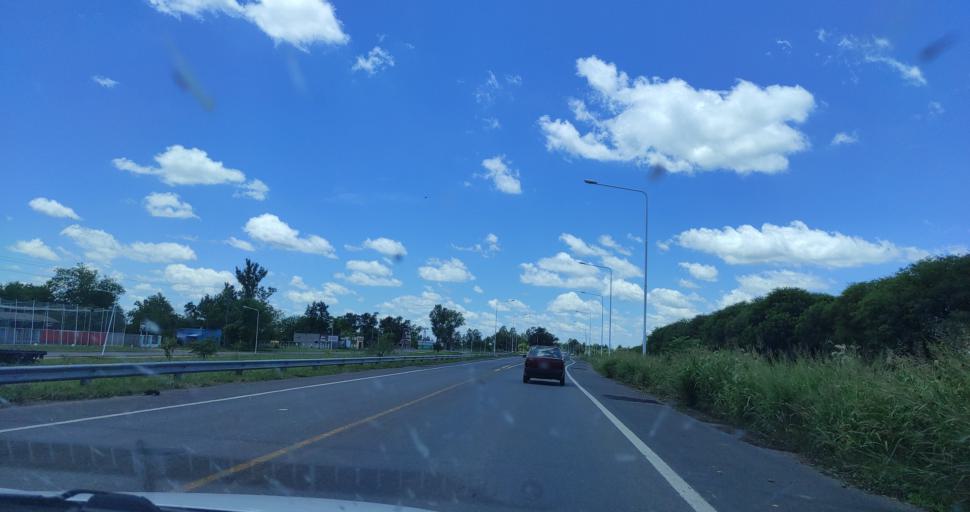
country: AR
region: Chaco
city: Avia Terai
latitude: -26.7030
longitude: -60.7313
